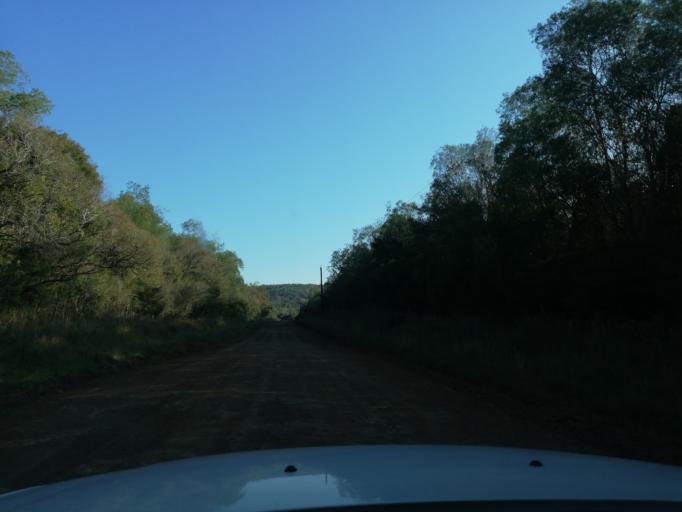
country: AR
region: Misiones
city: Cerro Cora
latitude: -27.6038
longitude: -55.7015
